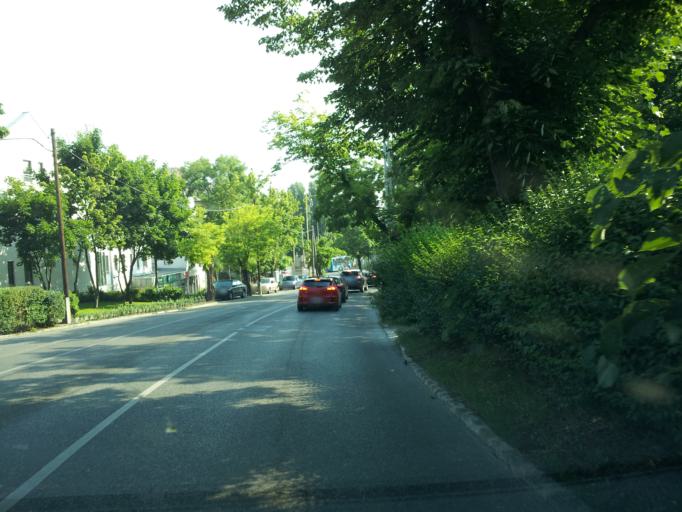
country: HU
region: Budapest
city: Budapest XII. keruelet
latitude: 47.4860
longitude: 19.0223
